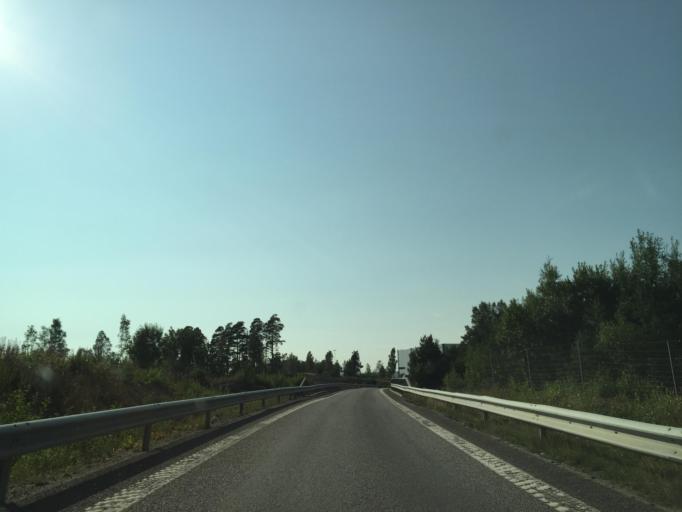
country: SE
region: Vaestra Goetaland
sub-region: Trollhattan
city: Trollhattan
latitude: 58.3389
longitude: 12.2657
